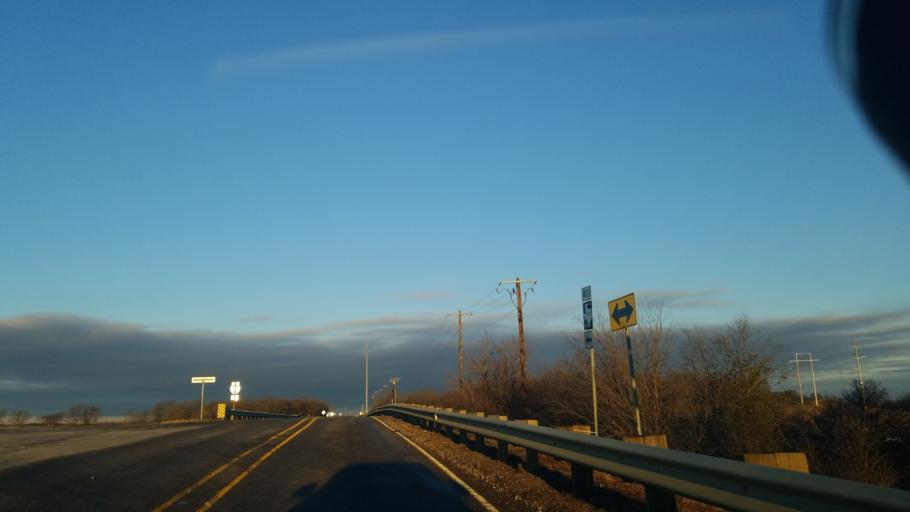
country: US
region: Texas
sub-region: Denton County
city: Argyle
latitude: 33.1712
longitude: -97.1799
